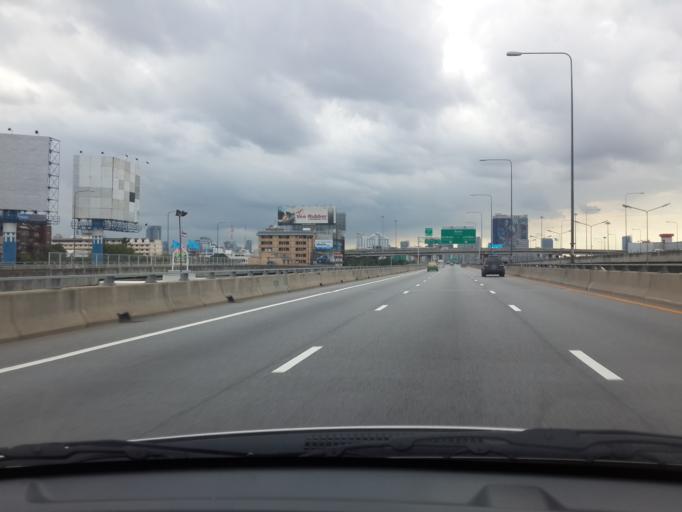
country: TH
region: Bangkok
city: Watthana
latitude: 13.7499
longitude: 100.5977
